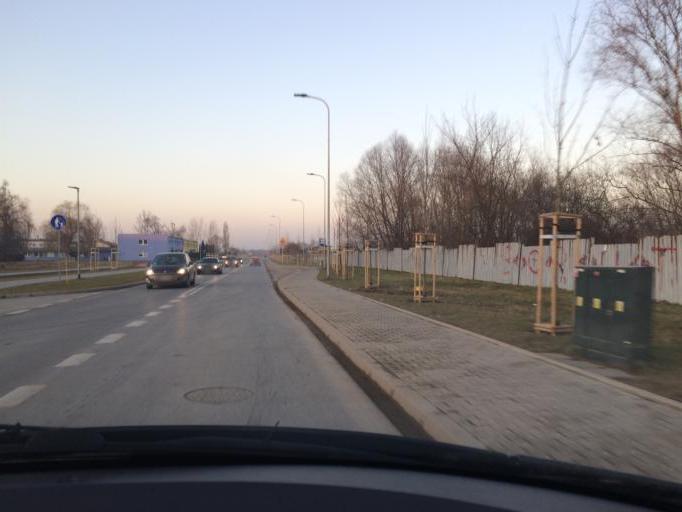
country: PL
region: Lesser Poland Voivodeship
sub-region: Powiat wielicki
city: Czarnochowice
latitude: 50.0284
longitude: 20.0517
